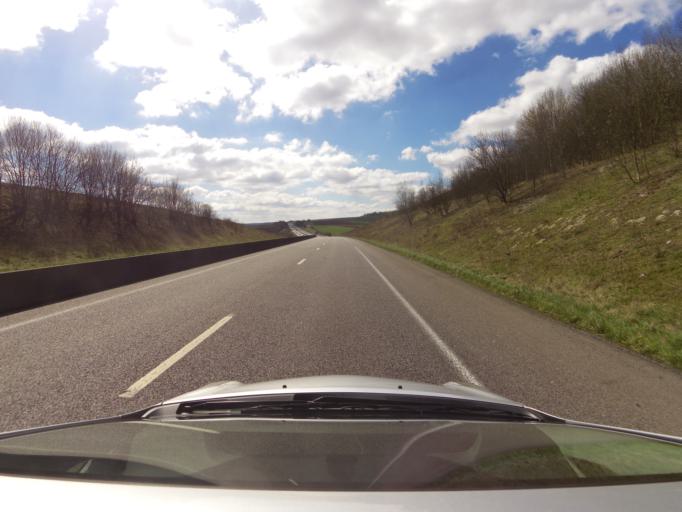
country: FR
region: Haute-Normandie
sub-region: Departement de la Seine-Maritime
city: Foucarmont
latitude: 49.8642
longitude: 1.5550
